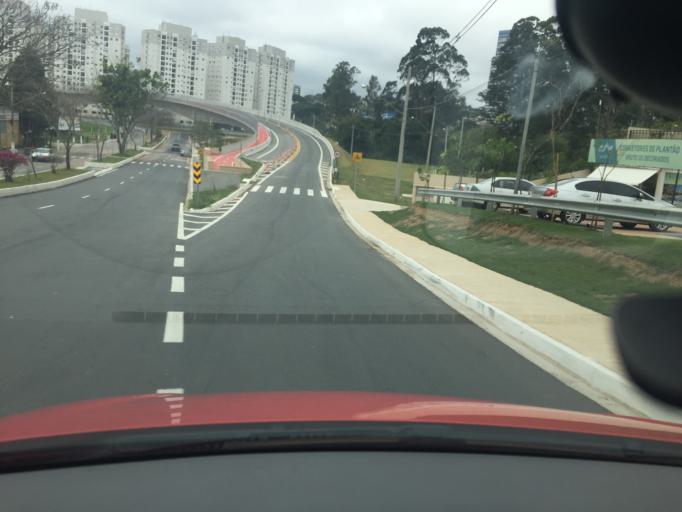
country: BR
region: Sao Paulo
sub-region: Jundiai
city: Jundiai
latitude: -23.1885
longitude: -46.9094
